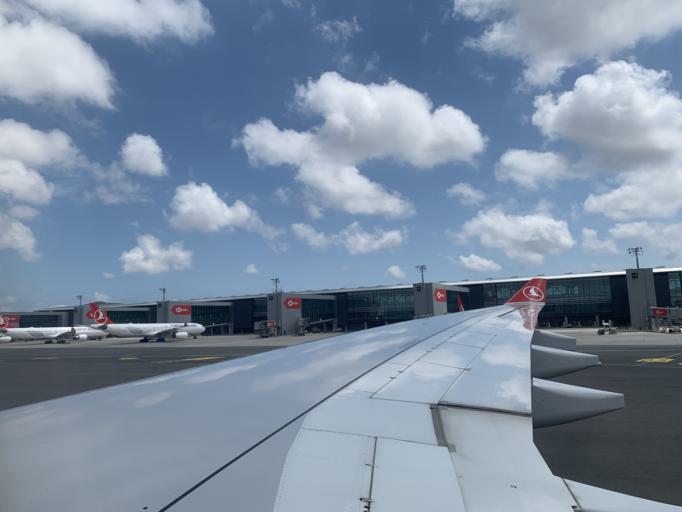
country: TR
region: Istanbul
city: Durusu
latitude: 41.2643
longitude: 28.7393
